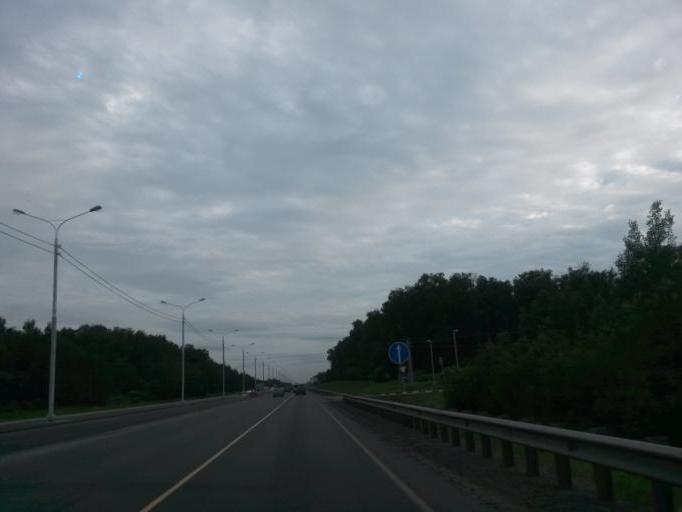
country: RU
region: Moskovskaya
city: L'vovskiy
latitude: 55.3251
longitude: 37.5608
